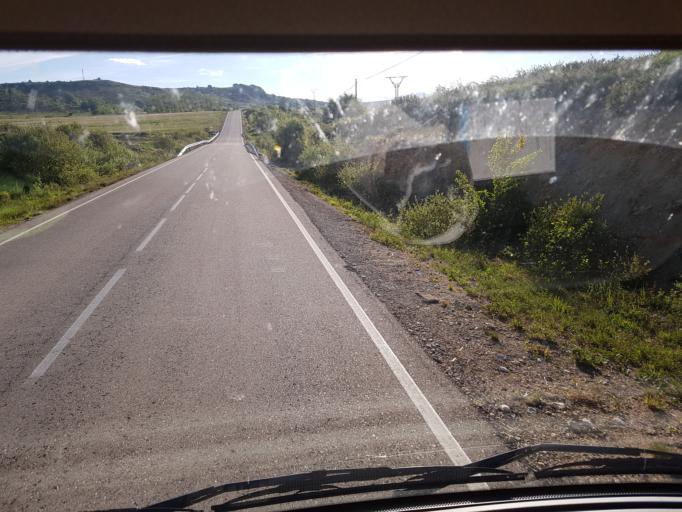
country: ES
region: Castille and Leon
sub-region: Provincia de Burgos
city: Arija
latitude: 42.9768
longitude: -3.8730
